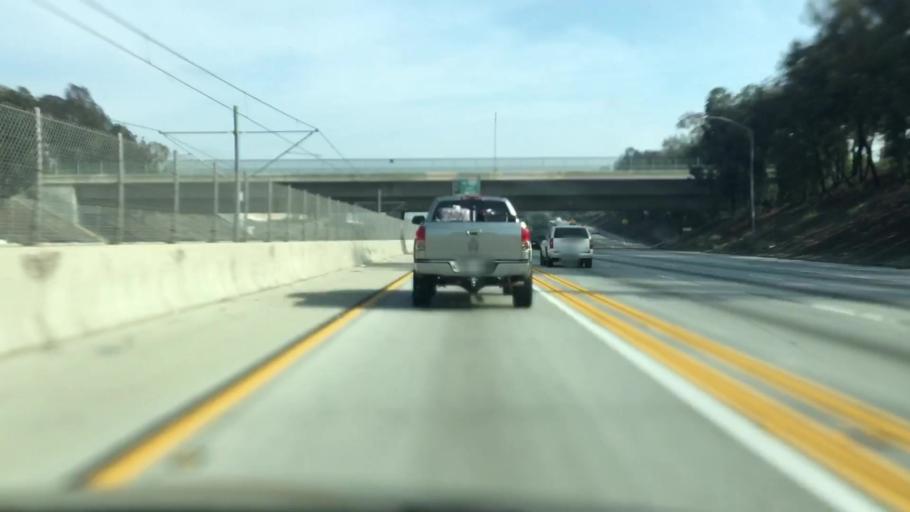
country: US
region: California
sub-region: Los Angeles County
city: Downey
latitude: 33.9130
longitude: -118.1310
